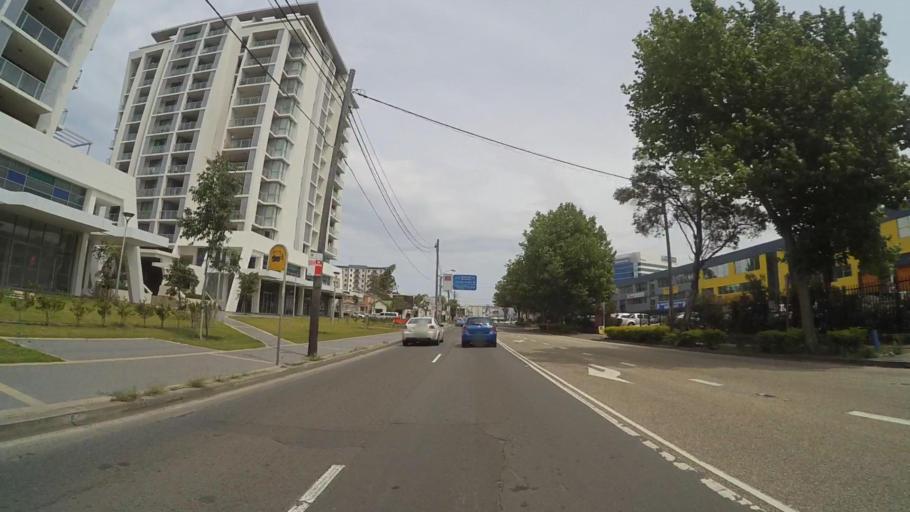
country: AU
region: New South Wales
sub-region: Botany Bay
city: Mascot
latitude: -33.9289
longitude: 151.1871
